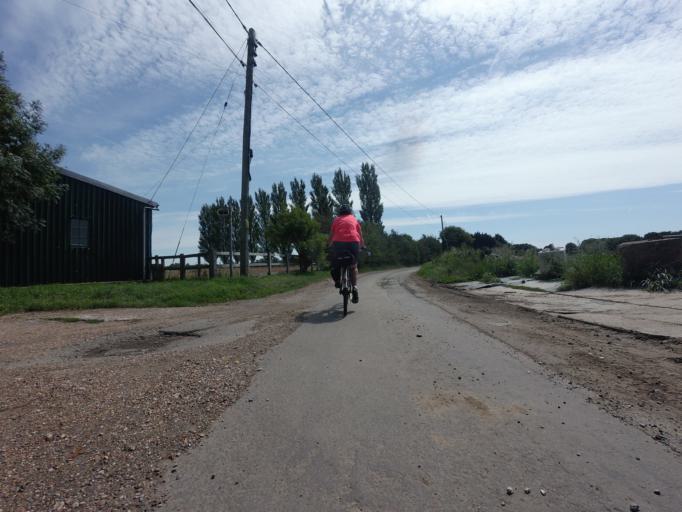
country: GB
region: England
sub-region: Kent
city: Stone
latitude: 51.0012
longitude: 0.8289
